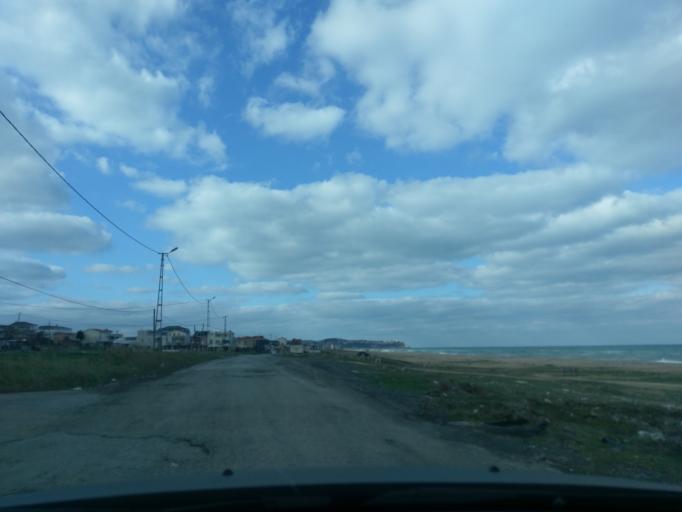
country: TR
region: Istanbul
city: Durusu
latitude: 41.3259
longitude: 28.7239
